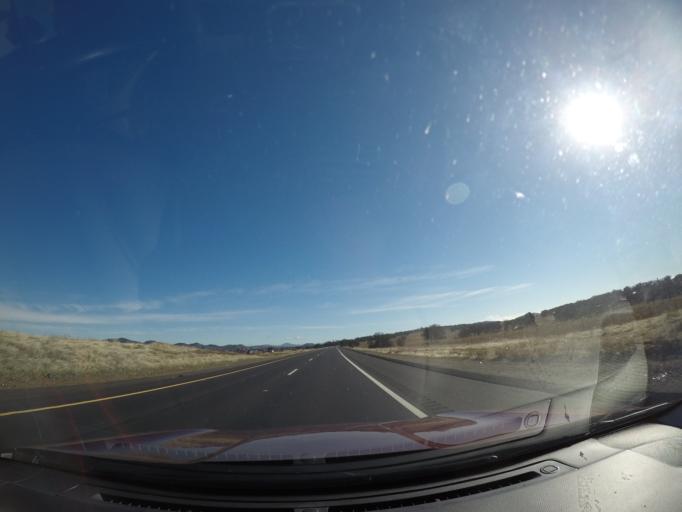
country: US
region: California
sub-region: Calaveras County
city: Copperopolis
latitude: 37.8449
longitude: -120.5498
